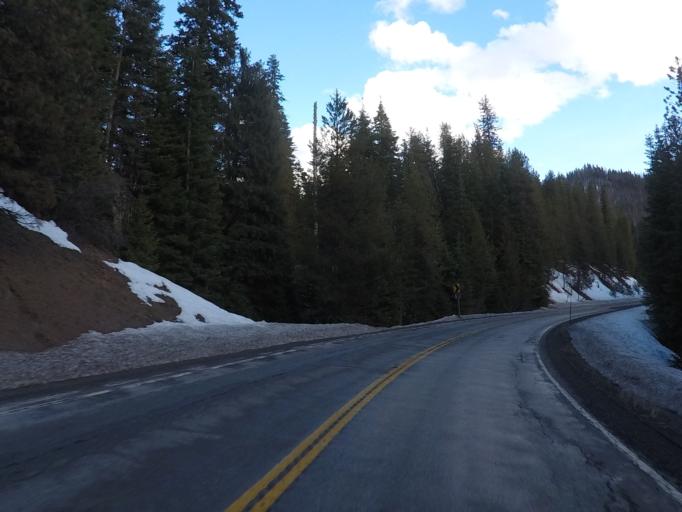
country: US
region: Montana
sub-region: Ravalli County
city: Hamilton
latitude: 46.5170
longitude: -114.7356
